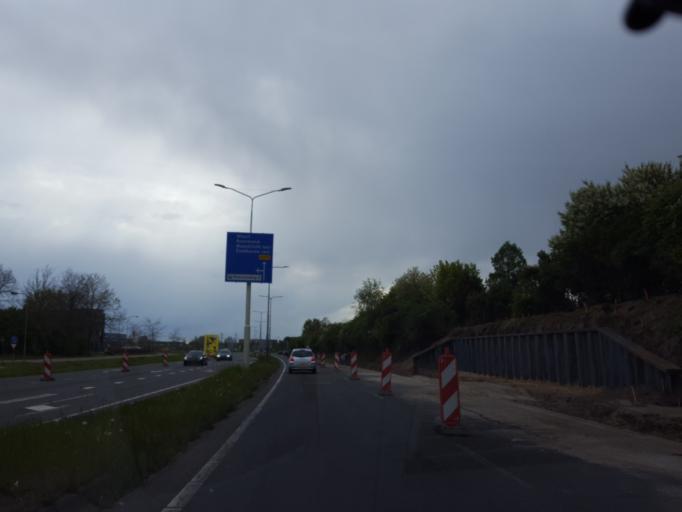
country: NL
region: Limburg
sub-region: Gemeente Nederweert
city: Nederweert
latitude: 51.2793
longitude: 5.7494
